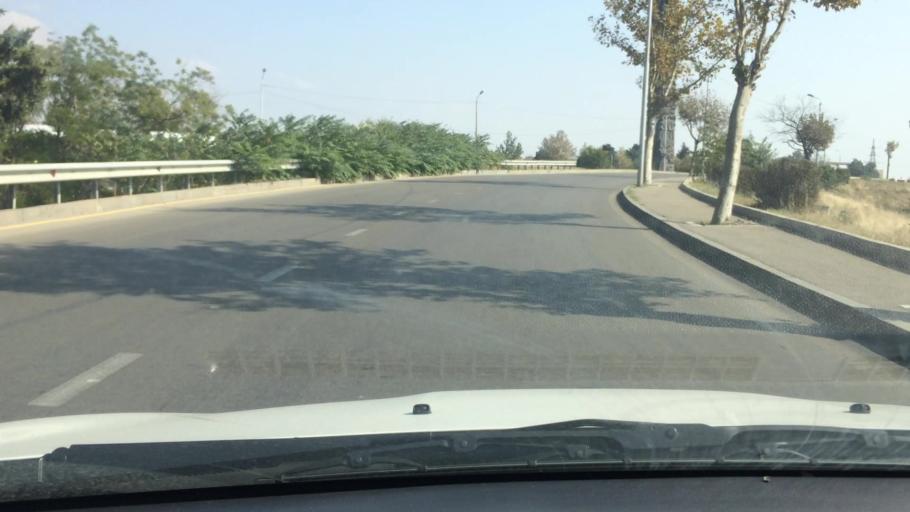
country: GE
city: Didi Lilo
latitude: 41.6923
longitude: 44.9510
